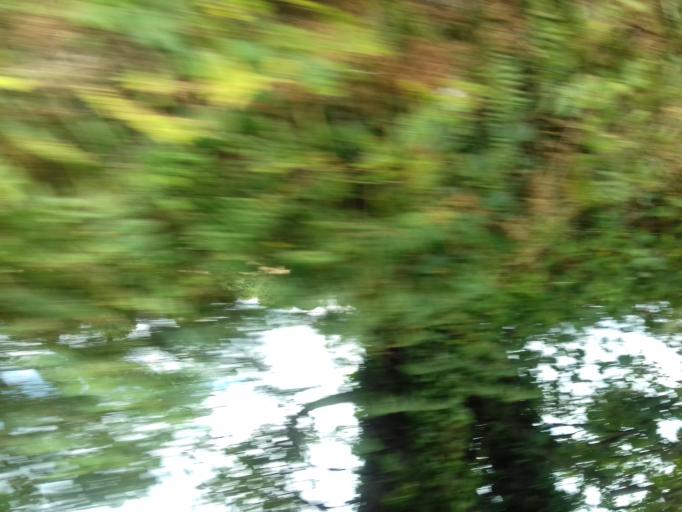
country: IE
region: Leinster
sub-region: Loch Garman
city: Enniscorthy
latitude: 52.5040
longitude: -6.5415
